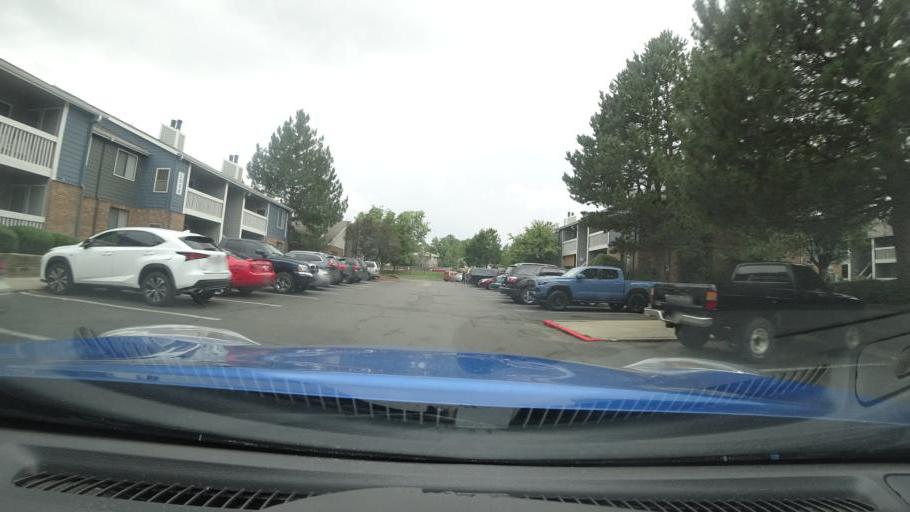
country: US
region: Colorado
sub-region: Adams County
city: Aurora
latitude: 39.6974
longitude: -104.8146
